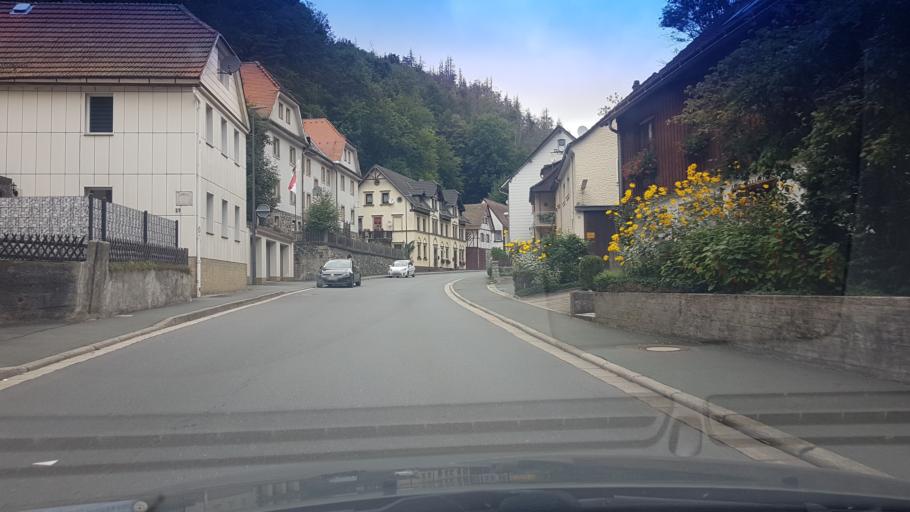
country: DE
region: Bavaria
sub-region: Upper Franconia
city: Bad Berneck im Fichtelgebirge
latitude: 50.0518
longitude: 11.6735
